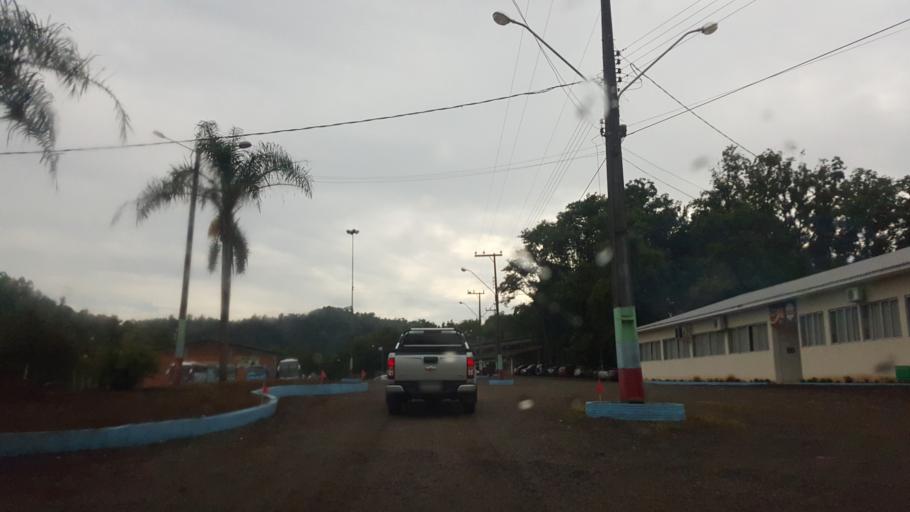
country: BR
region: Rio Grande do Sul
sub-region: Frederico Westphalen
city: Frederico Westphalen
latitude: -27.0909
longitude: -53.3830
